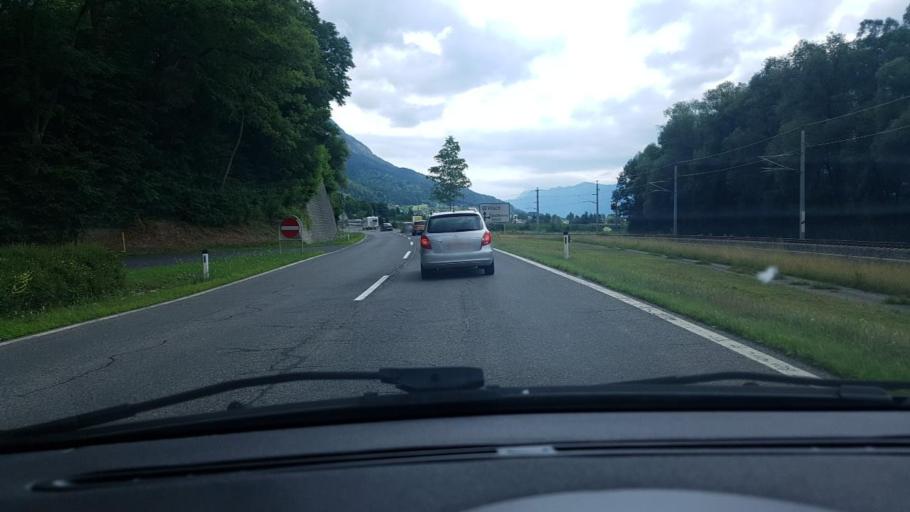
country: AT
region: Carinthia
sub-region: Politischer Bezirk Villach Land
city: Feistritz an der Gail
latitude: 46.5931
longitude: 13.6074
